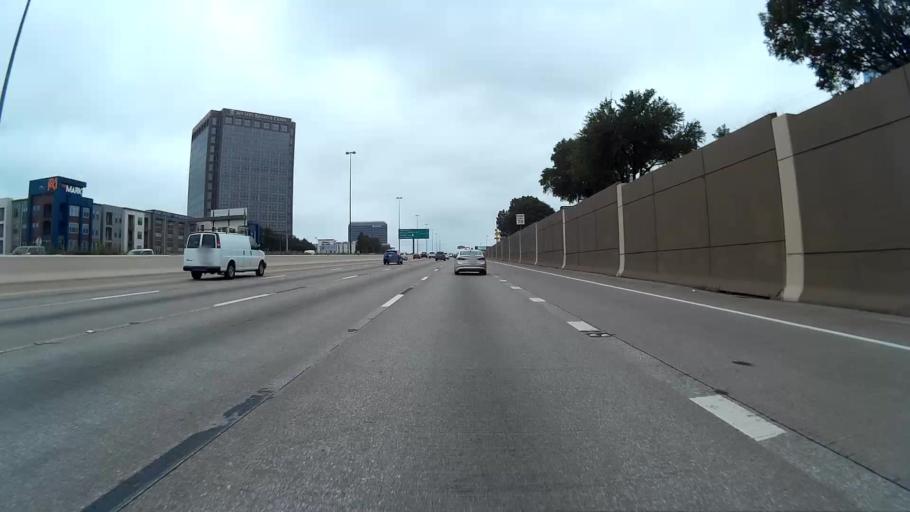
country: US
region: Texas
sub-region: Dallas County
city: University Park
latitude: 32.8909
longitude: -96.7694
